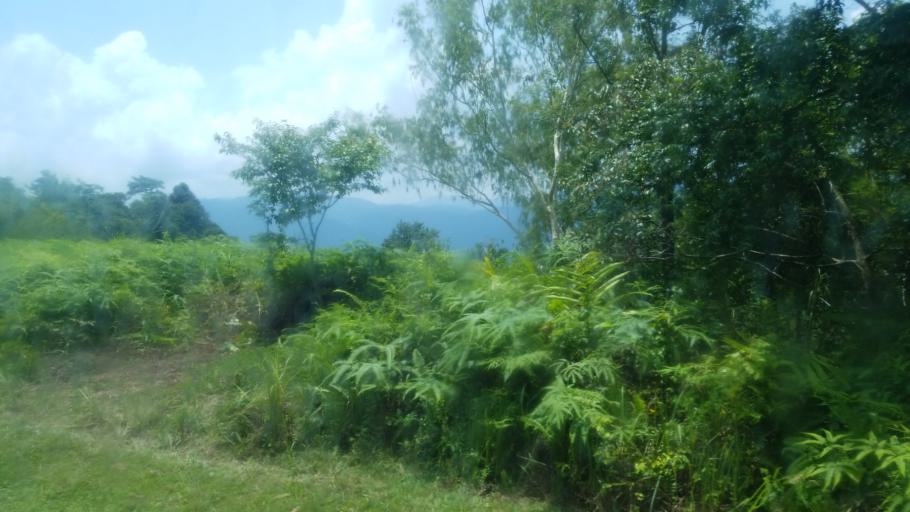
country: TH
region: Narathiwat
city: Sukhirin
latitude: 5.6363
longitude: 101.6938
